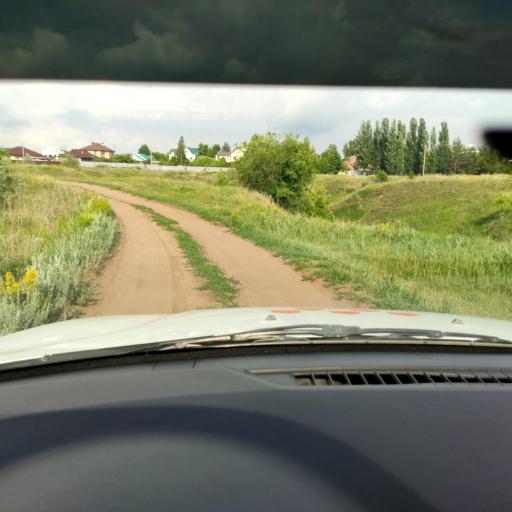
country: RU
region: Samara
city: Podstepki
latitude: 53.6132
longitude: 49.0307
